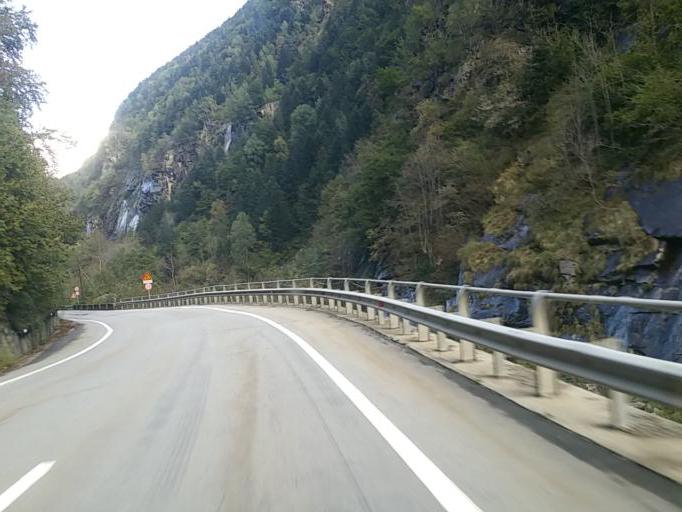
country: IT
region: Piedmont
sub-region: Provincia Verbano-Cusio-Ossola
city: Trasquera
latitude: 46.1987
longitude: 8.1653
